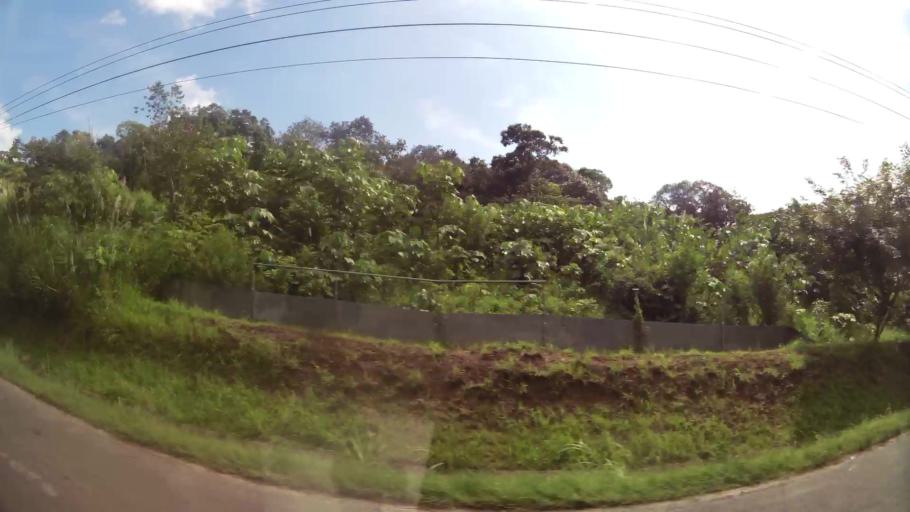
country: PA
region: Panama
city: Las Cumbres
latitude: 9.0411
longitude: -79.5664
